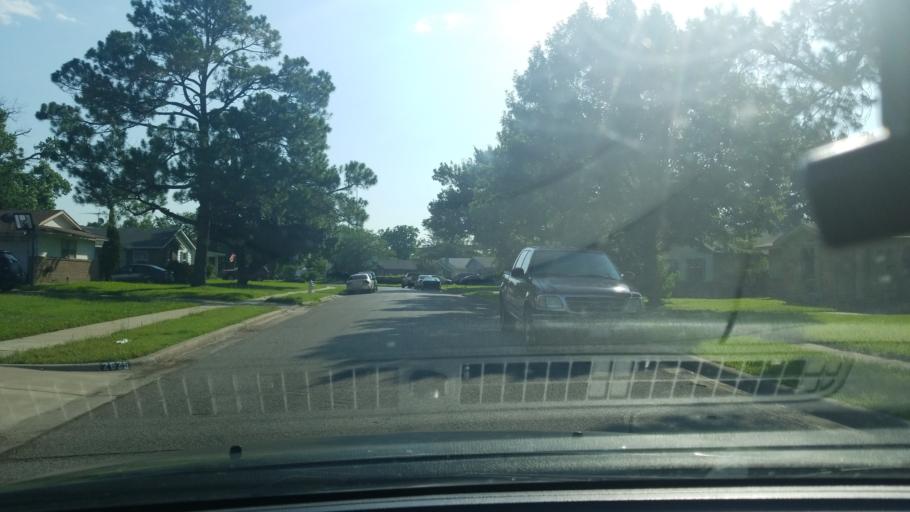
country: US
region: Texas
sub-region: Dallas County
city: Mesquite
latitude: 32.8229
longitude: -96.6337
